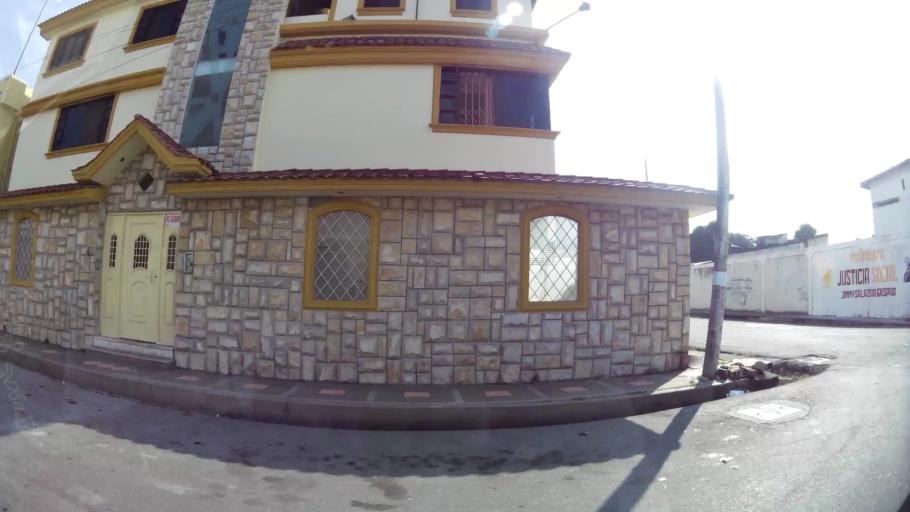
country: EC
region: Guayas
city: Guayaquil
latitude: -2.1878
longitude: -79.9036
